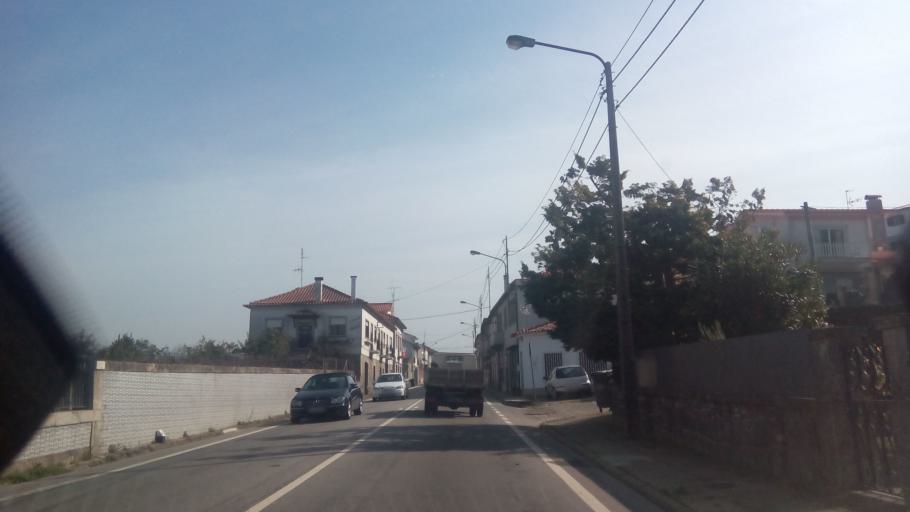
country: PT
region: Viana do Castelo
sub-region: Viana do Castelo
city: Darque
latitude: 41.6825
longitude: -8.7882
